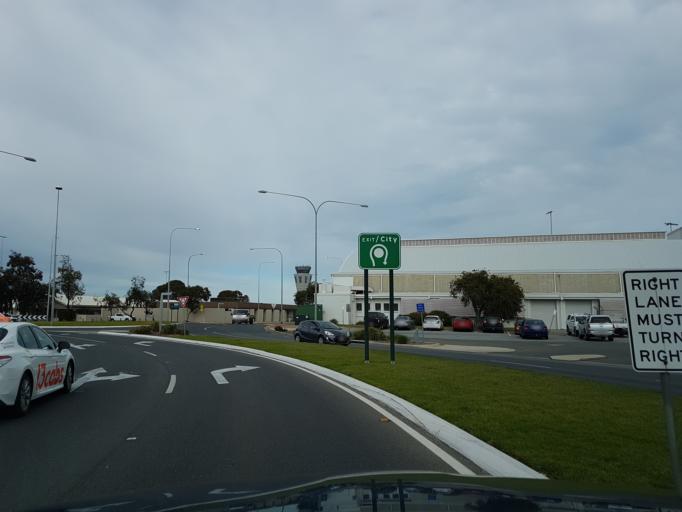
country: AU
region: South Australia
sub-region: City of West Torrens
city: Plympton
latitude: -34.9388
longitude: 138.5343
